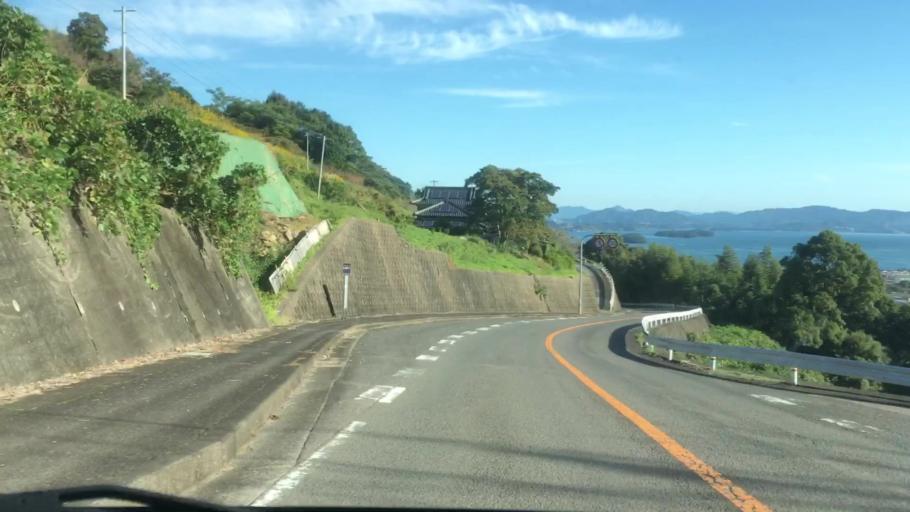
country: JP
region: Nagasaki
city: Sasebo
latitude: 32.9957
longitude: 129.7247
